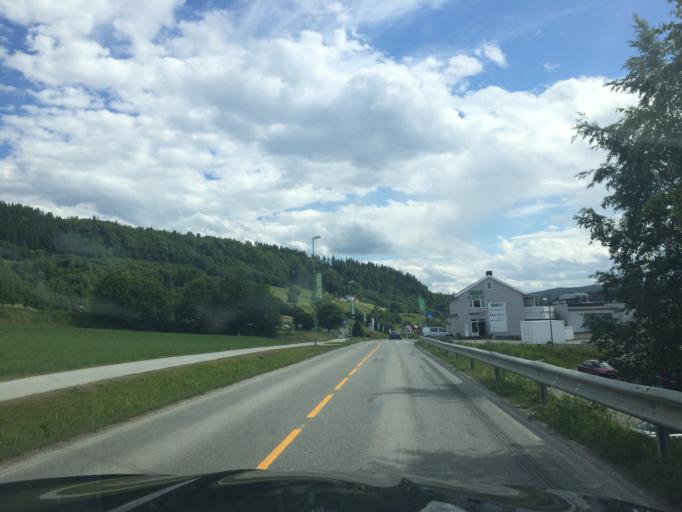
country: NO
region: Sor-Trondelag
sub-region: Selbu
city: Mebonden
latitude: 63.2203
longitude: 11.0393
